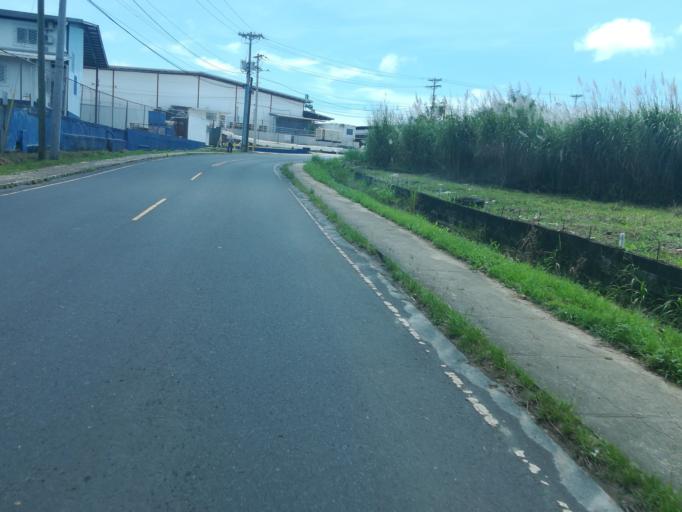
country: PA
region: Panama
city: Tocumen
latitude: 9.0904
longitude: -79.3992
